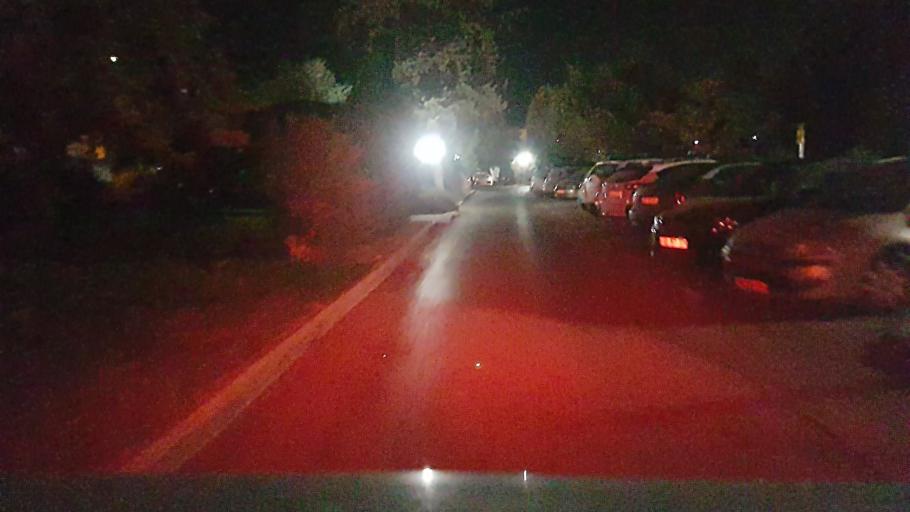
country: IL
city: Nirit
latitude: 32.1374
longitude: 34.9725
